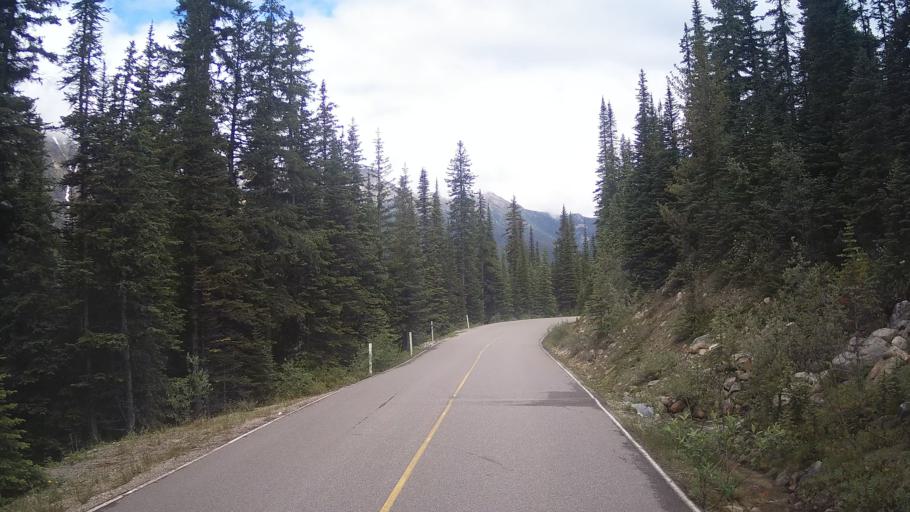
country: CA
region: Alberta
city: Jasper Park Lodge
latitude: 52.6962
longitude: -118.0582
